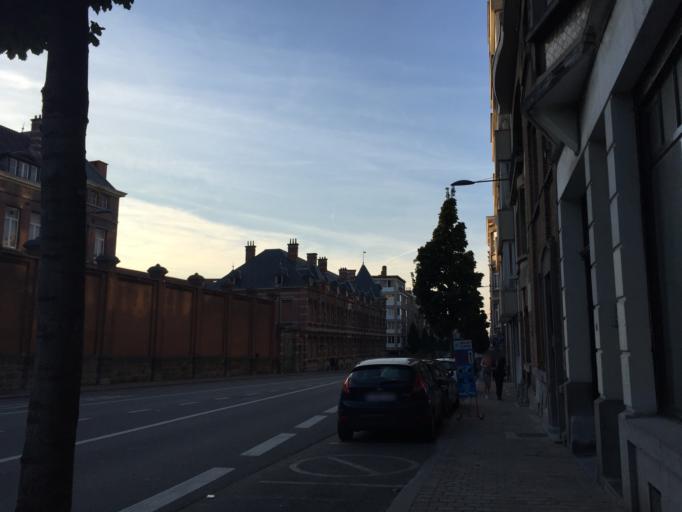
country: BE
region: Brussels Capital
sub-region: Bruxelles-Capitale
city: Brussels
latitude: 50.8232
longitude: 4.3874
